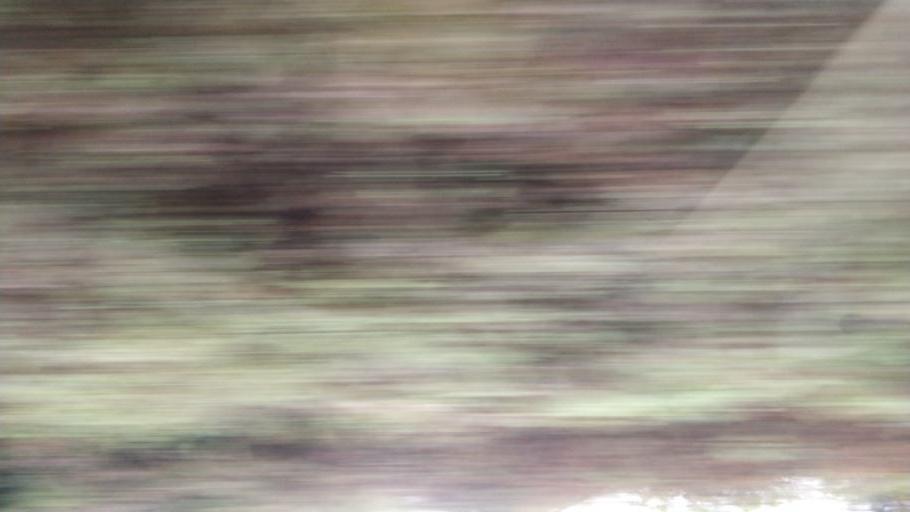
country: GB
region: England
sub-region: Lancashire
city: Appley Bridge
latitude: 53.5746
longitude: -2.7138
